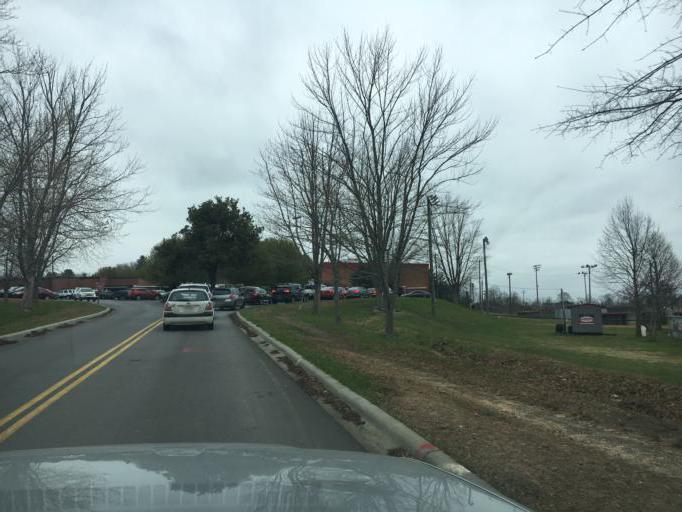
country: US
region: North Carolina
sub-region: Buncombe County
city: Woodfin
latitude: 35.6166
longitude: -82.6289
